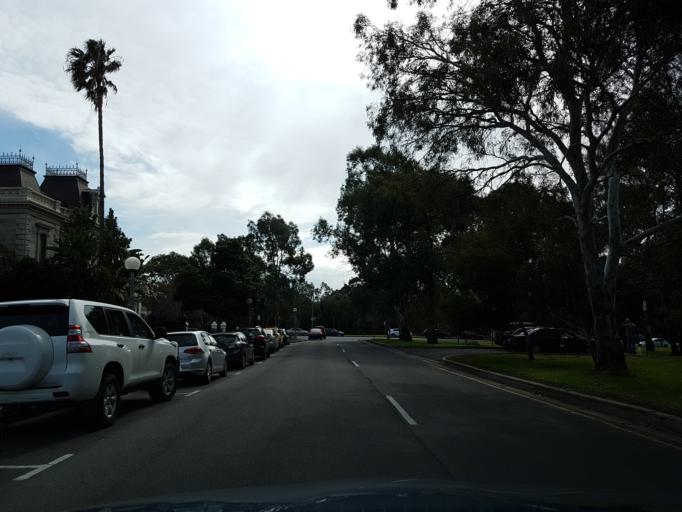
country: AU
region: South Australia
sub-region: Adelaide
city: Adelaide
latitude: -34.9286
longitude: 138.6152
